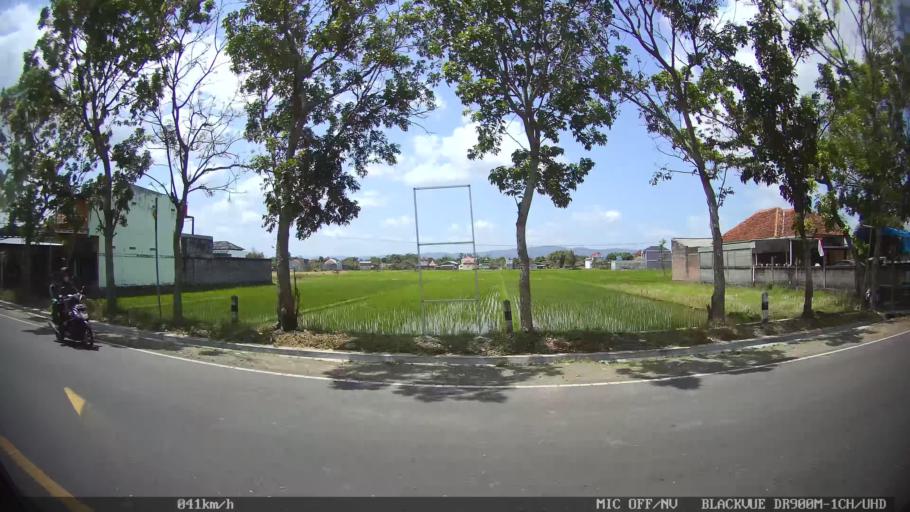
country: ID
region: Daerah Istimewa Yogyakarta
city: Bantul
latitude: -7.9008
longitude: 110.3459
